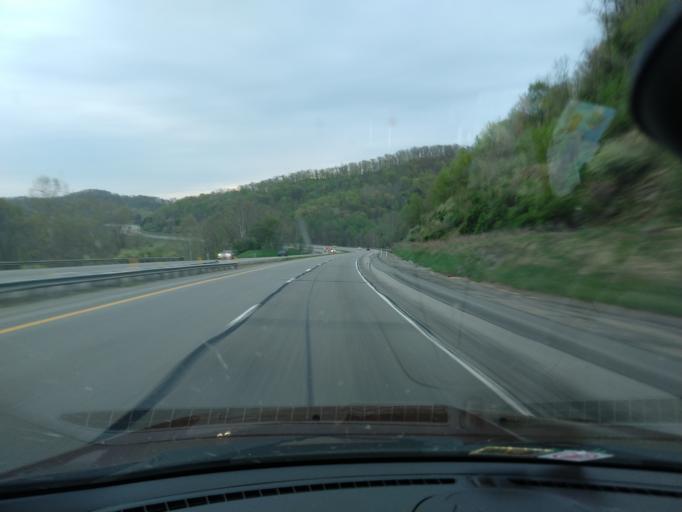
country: US
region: West Virginia
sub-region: Lewis County
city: Weston
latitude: 38.9172
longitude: -80.5666
